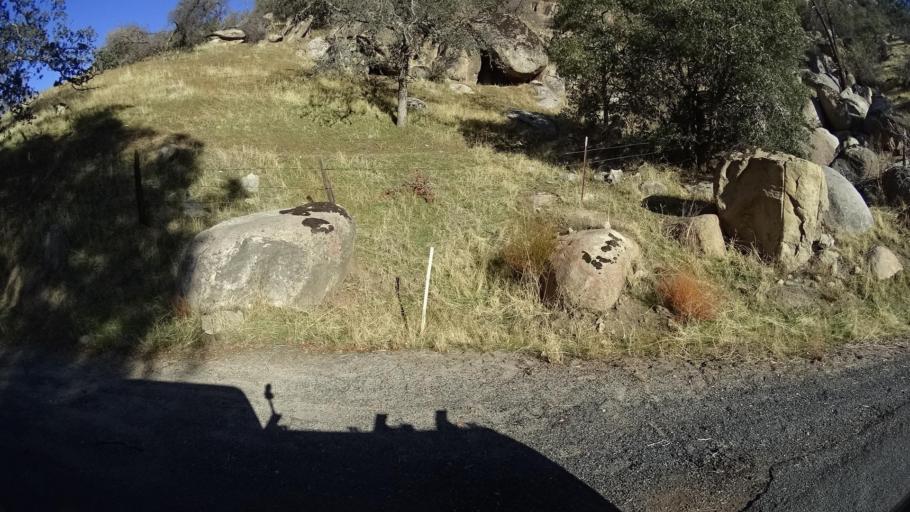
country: US
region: California
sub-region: Kern County
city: Alta Sierra
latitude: 35.7869
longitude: -118.7856
